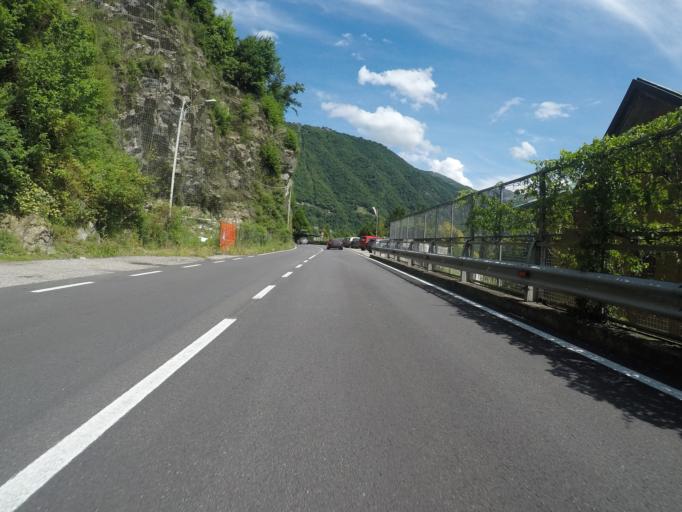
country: IT
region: Lombardy
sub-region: Provincia di Como
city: Argegno
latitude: 45.9361
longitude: 9.1283
